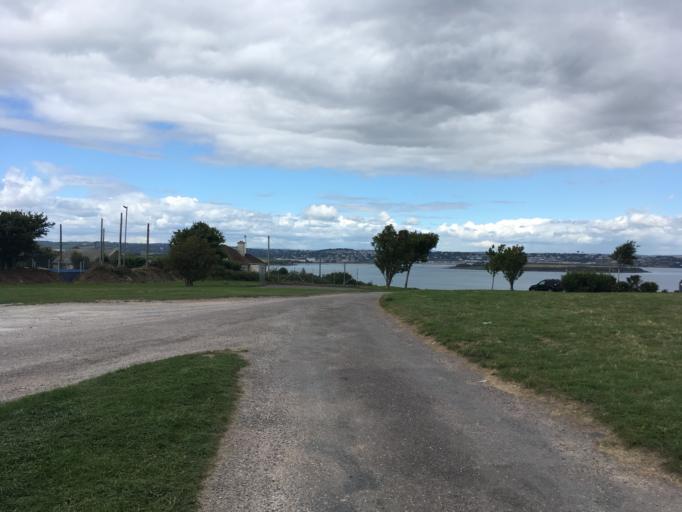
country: IE
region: Munster
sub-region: County Cork
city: Crosshaven
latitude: 51.8085
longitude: -8.2807
